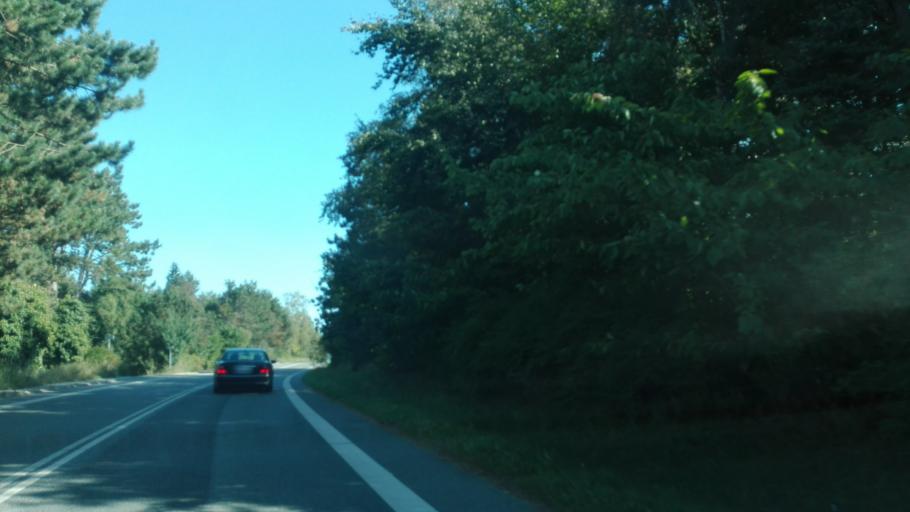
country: DK
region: Central Jutland
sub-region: Syddjurs Kommune
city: Ebeltoft
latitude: 56.2148
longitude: 10.6921
